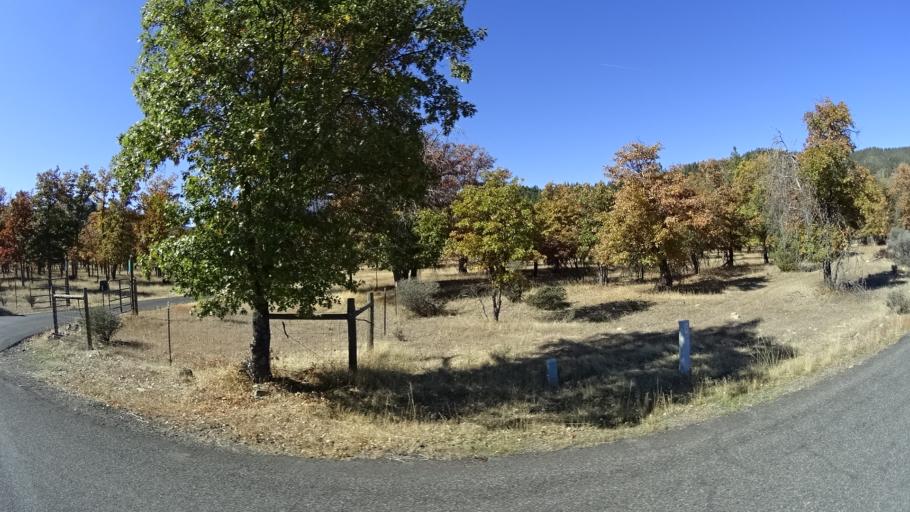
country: US
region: California
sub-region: Siskiyou County
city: Yreka
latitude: 41.5463
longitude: -122.9356
